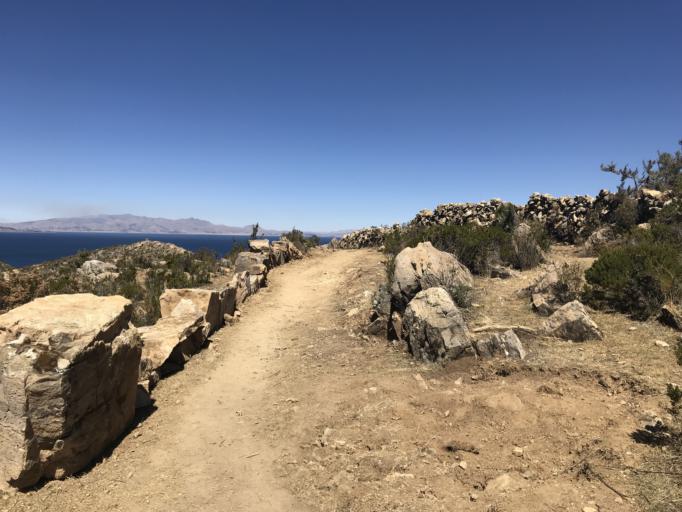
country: BO
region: La Paz
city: Yumani
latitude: -16.0460
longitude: -69.1464
